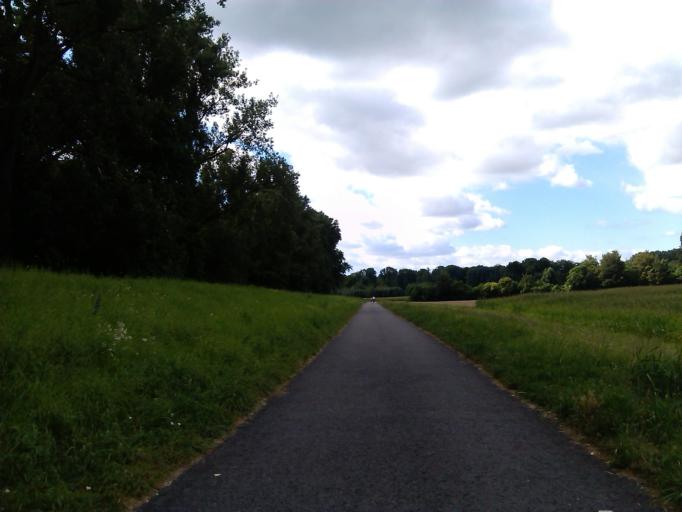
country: DE
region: Rheinland-Pfalz
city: Altrip
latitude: 49.4251
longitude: 8.4952
